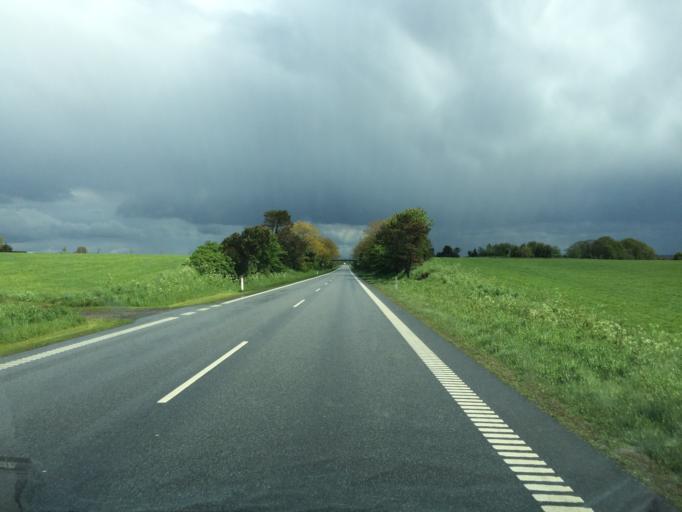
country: DK
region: Central Jutland
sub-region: Skive Kommune
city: Hojslev
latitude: 56.5954
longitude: 9.2338
